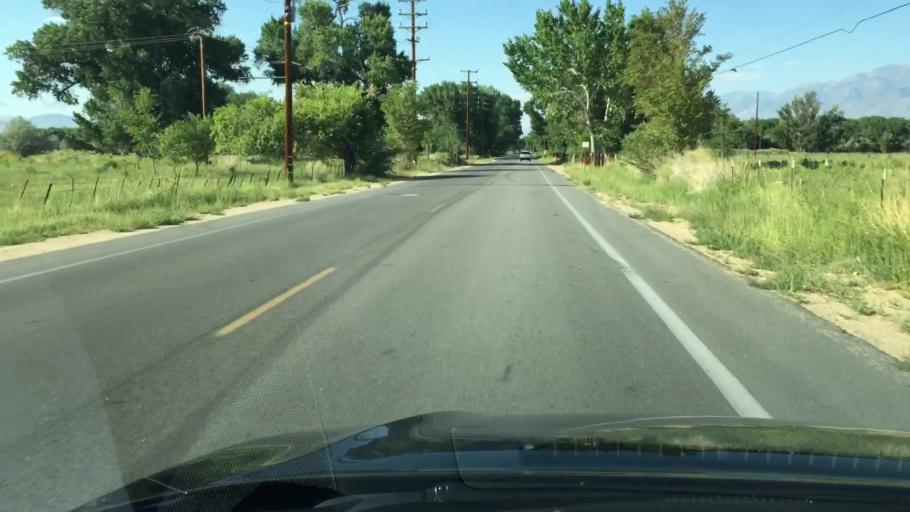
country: US
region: California
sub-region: Inyo County
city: Bishop
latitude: 37.3534
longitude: -118.4046
